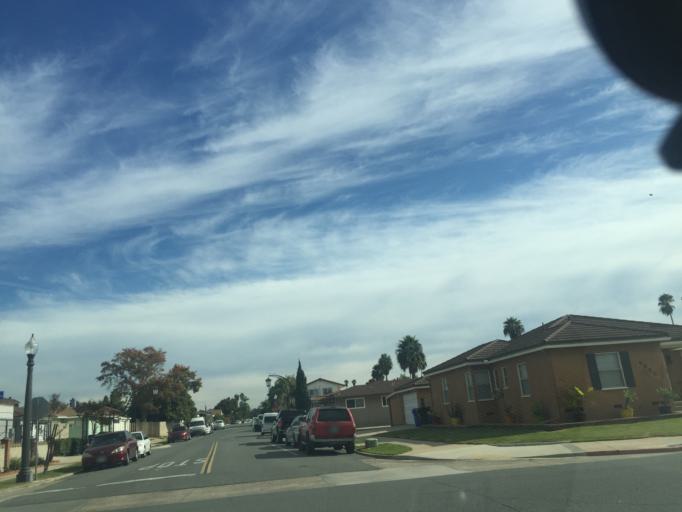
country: US
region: California
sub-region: San Diego County
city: Lemon Grove
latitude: 32.7609
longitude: -117.0890
